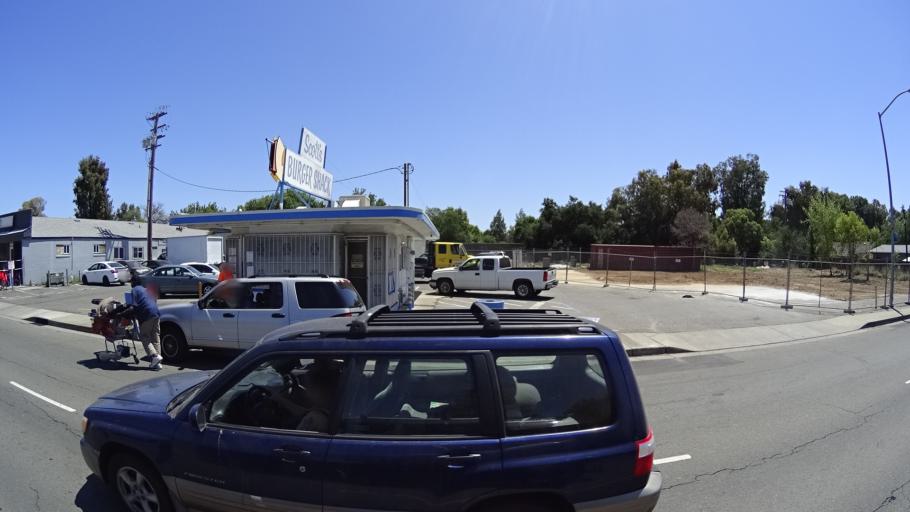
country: US
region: California
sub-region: Sacramento County
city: Parkway
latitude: 38.5362
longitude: -121.4747
